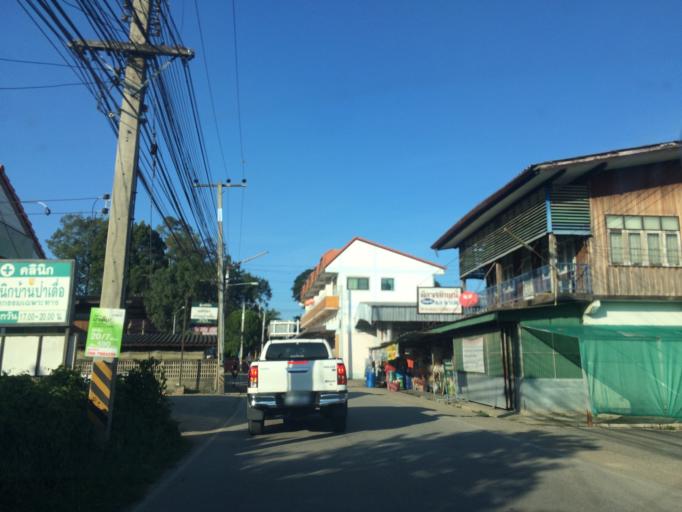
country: TH
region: Chiang Mai
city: Saraphi
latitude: 18.6786
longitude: 98.9846
